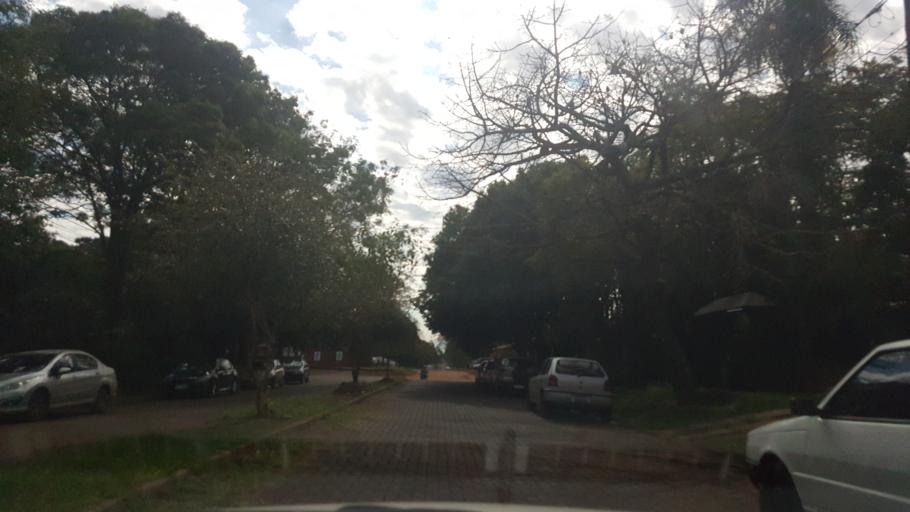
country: AR
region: Misiones
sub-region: Departamento de Capital
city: Posadas
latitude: -27.3658
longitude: -55.9201
